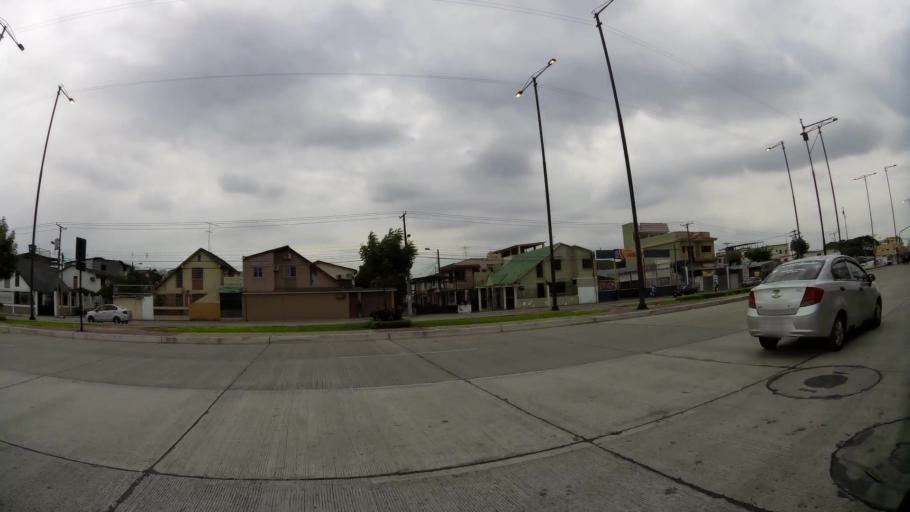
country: EC
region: Guayas
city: Eloy Alfaro
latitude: -2.1138
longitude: -79.8988
